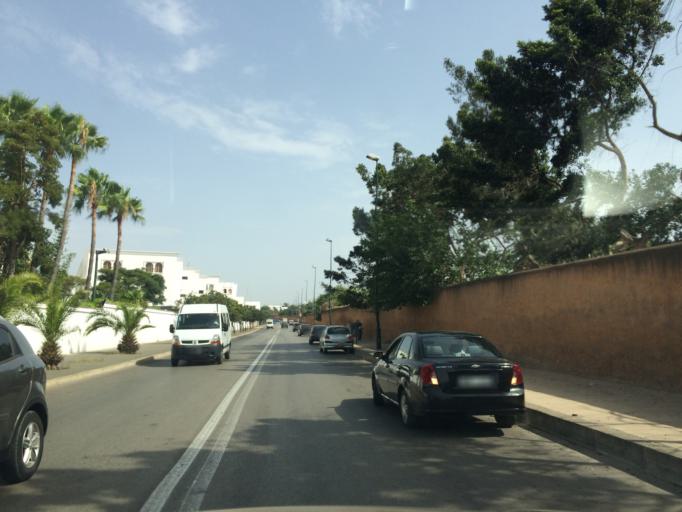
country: MA
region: Rabat-Sale-Zemmour-Zaer
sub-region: Rabat
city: Rabat
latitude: 34.0117
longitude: -6.8316
